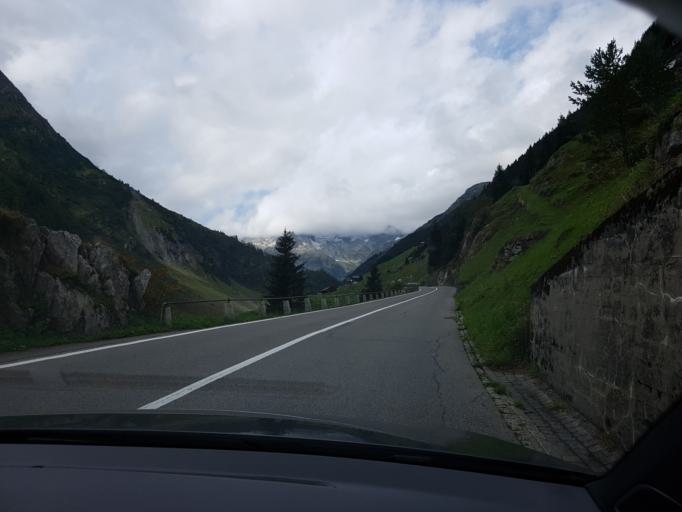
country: CH
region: Uri
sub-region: Uri
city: Andermatt
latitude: 46.7340
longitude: 8.5318
